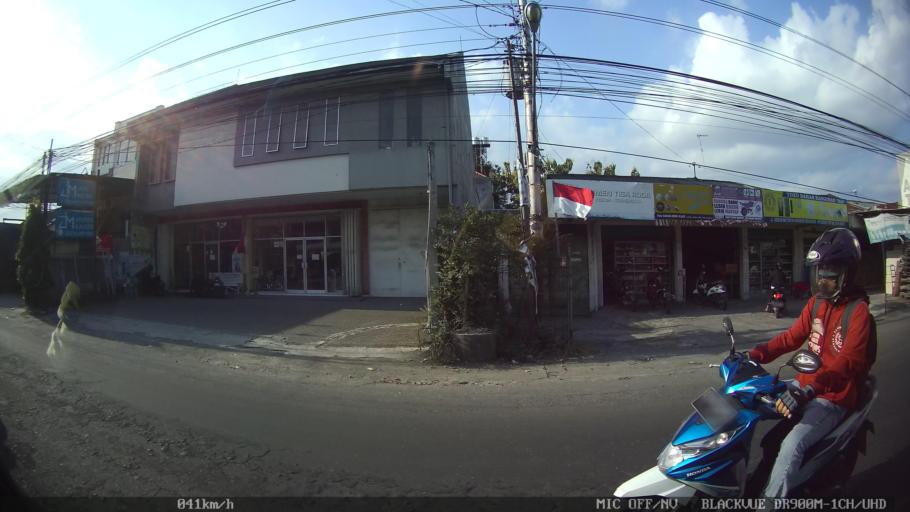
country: ID
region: Daerah Istimewa Yogyakarta
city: Yogyakarta
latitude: -7.7785
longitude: 110.3402
